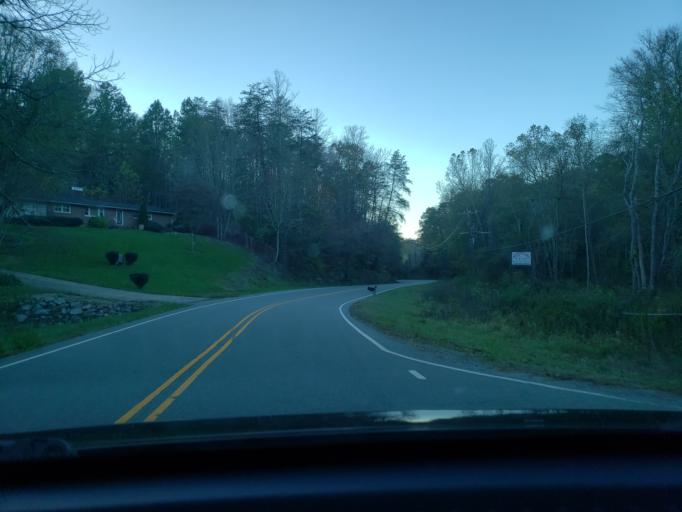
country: US
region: North Carolina
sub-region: Stokes County
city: Danbury
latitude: 36.3853
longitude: -80.1886
